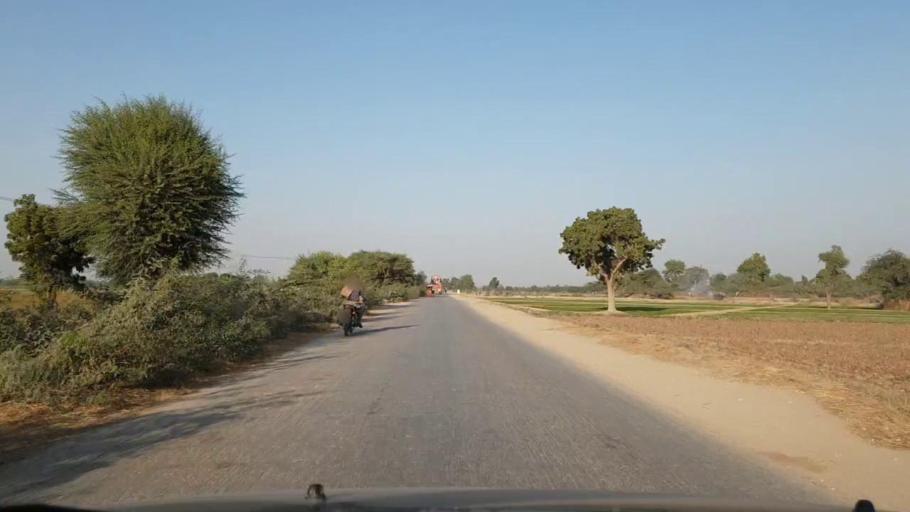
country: PK
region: Sindh
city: Chambar
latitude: 25.2220
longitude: 68.7819
